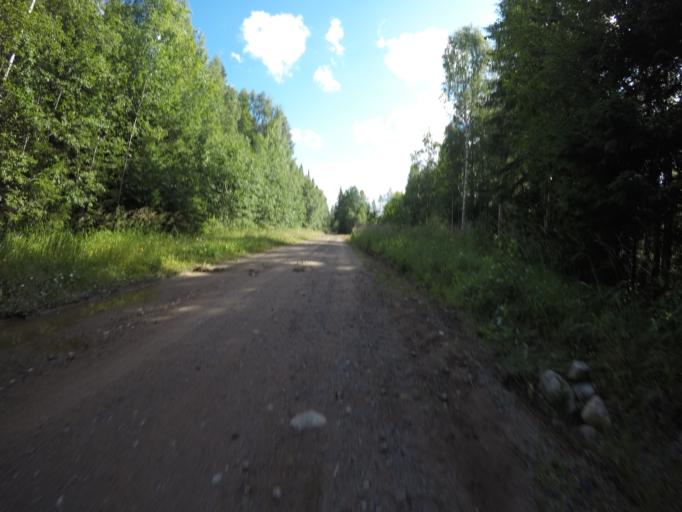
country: SE
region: OErebro
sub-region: Hallefors Kommun
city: Haellefors
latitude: 60.0001
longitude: 14.6061
